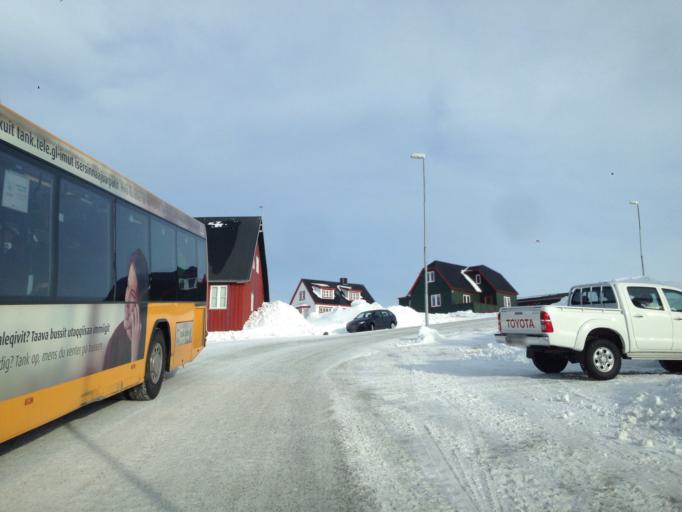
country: GL
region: Sermersooq
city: Nuuk
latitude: 64.1802
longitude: -51.7370
